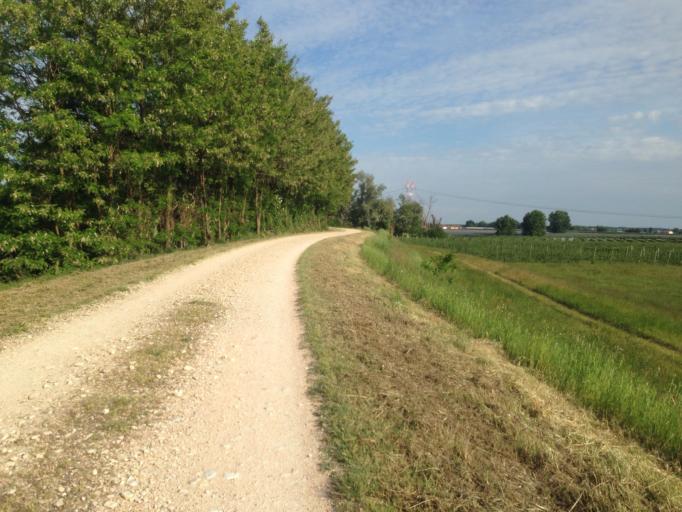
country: IT
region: Veneto
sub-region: Provincia di Verona
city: Zevio
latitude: 45.3710
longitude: 11.1682
